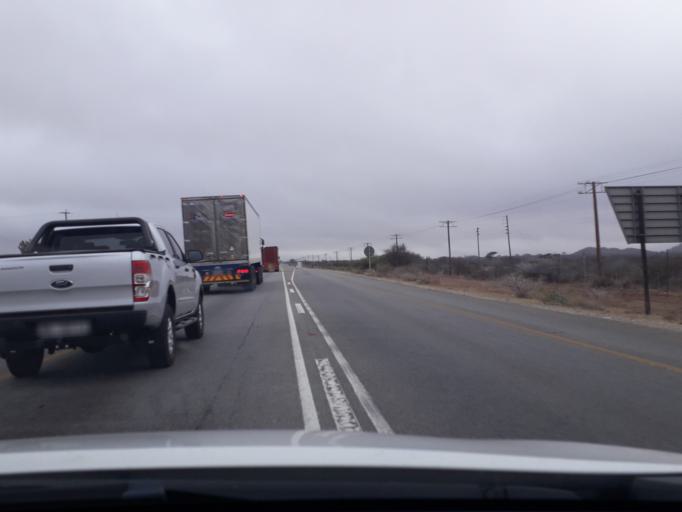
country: ZA
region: Limpopo
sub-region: Capricorn District Municipality
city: Mankoeng
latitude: -23.5222
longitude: 29.7082
